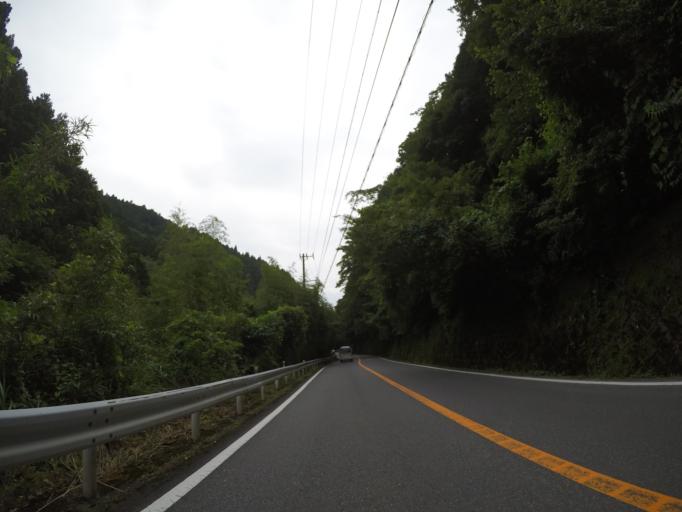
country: JP
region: Shizuoka
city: Fujinomiya
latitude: 35.1974
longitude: 138.5302
